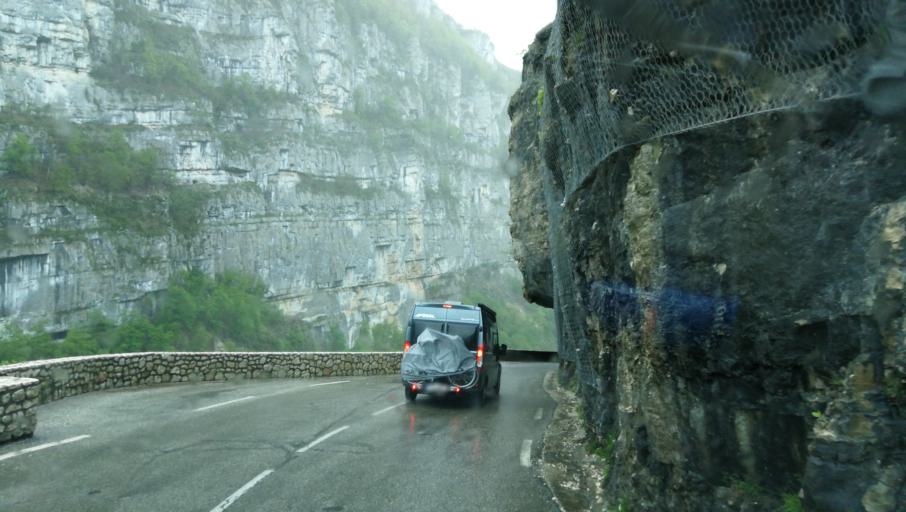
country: FR
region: Rhone-Alpes
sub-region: Departement de l'Isere
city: Meaudre
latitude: 45.0735
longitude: 5.4470
